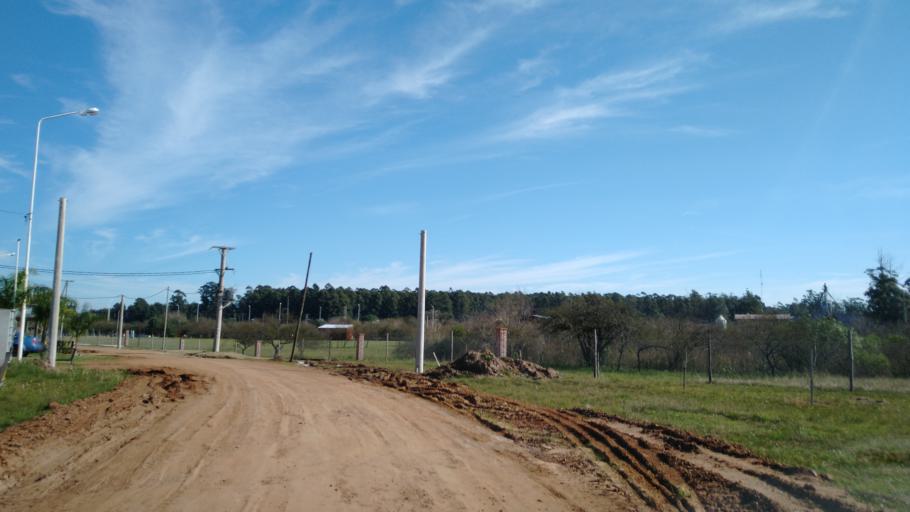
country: AR
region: Entre Rios
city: Chajari
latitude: -30.7411
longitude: -58.0120
